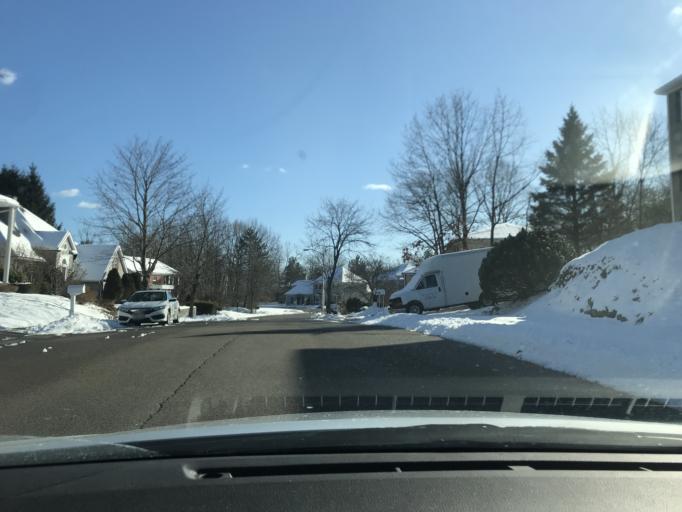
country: US
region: Massachusetts
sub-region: Essex County
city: Saugus
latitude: 42.4825
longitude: -71.0156
